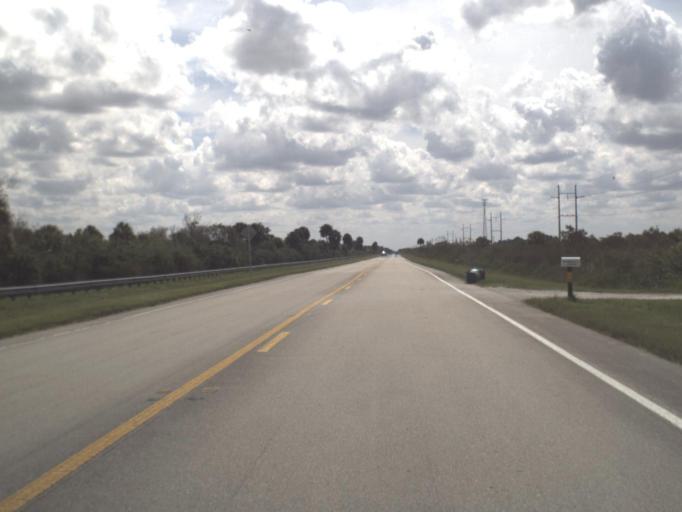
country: US
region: Florida
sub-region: Collier County
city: Immokalee
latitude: 26.1440
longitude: -81.3450
